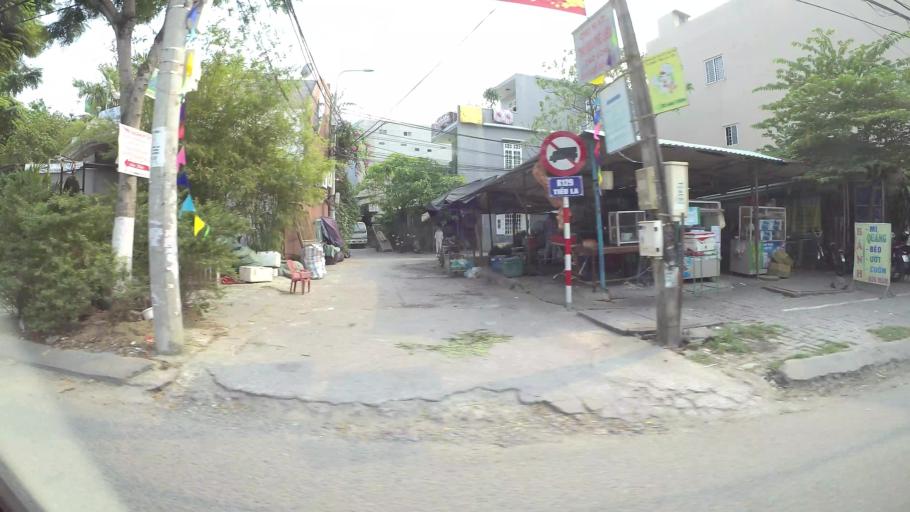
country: VN
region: Da Nang
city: Son Tra
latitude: 16.0447
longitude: 108.2168
